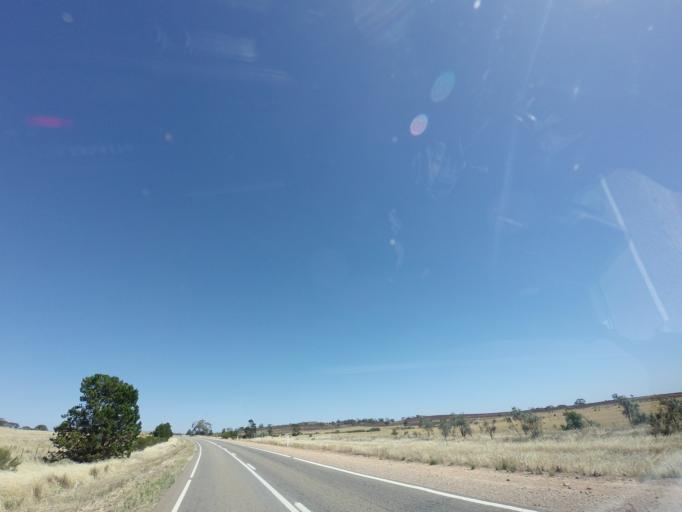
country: AU
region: South Australia
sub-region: Peterborough
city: Peterborough
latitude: -32.9094
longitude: 138.7613
